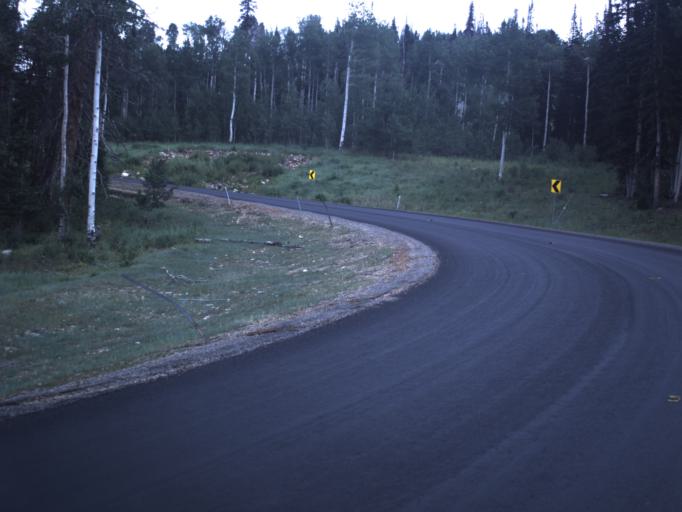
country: US
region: Utah
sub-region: Summit County
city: Francis
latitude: 40.4943
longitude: -111.0373
